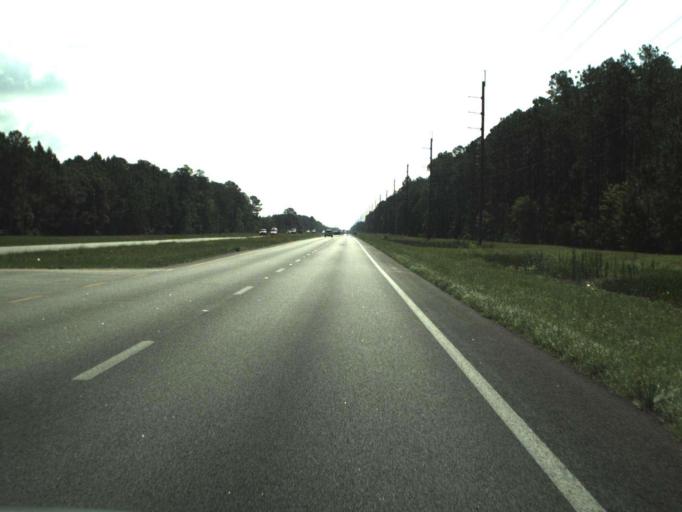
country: US
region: Florida
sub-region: Volusia County
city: Samsula-Spruce Creek
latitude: 29.0118
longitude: -81.0310
